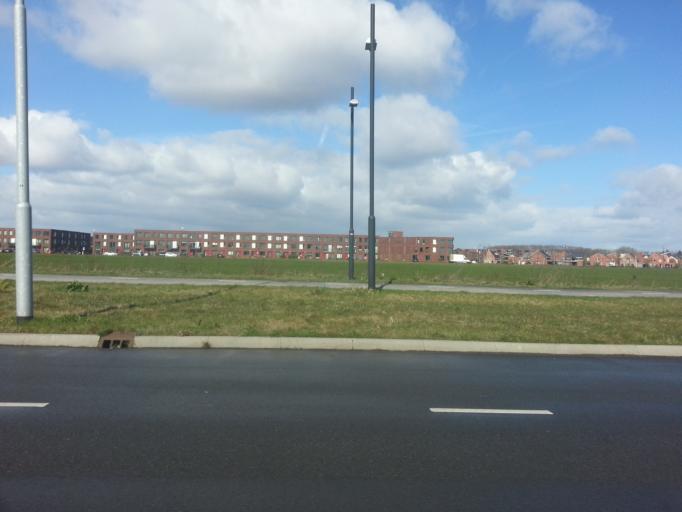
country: NL
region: North Brabant
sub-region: Gemeente Eindhoven
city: Meerhoven
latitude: 51.4347
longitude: 5.4209
